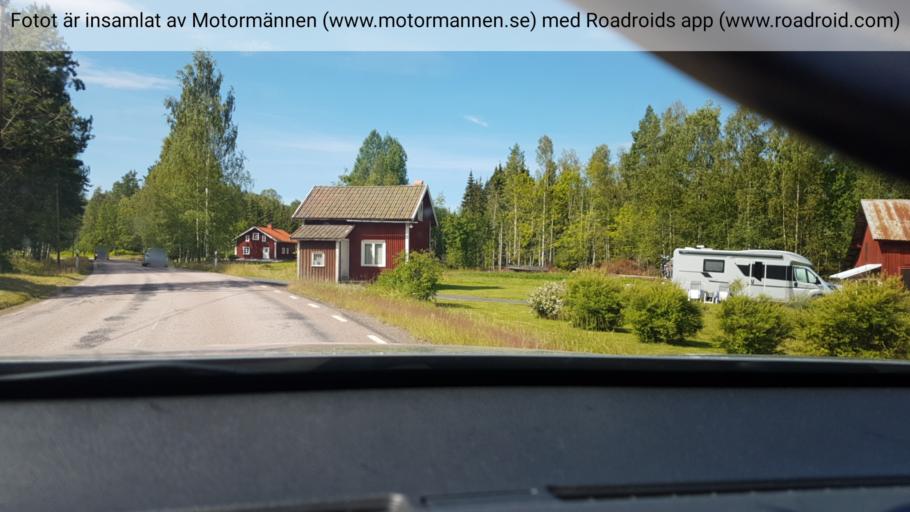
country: SE
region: Vaermland
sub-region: Sunne Kommun
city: Sunne
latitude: 59.8705
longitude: 13.2359
